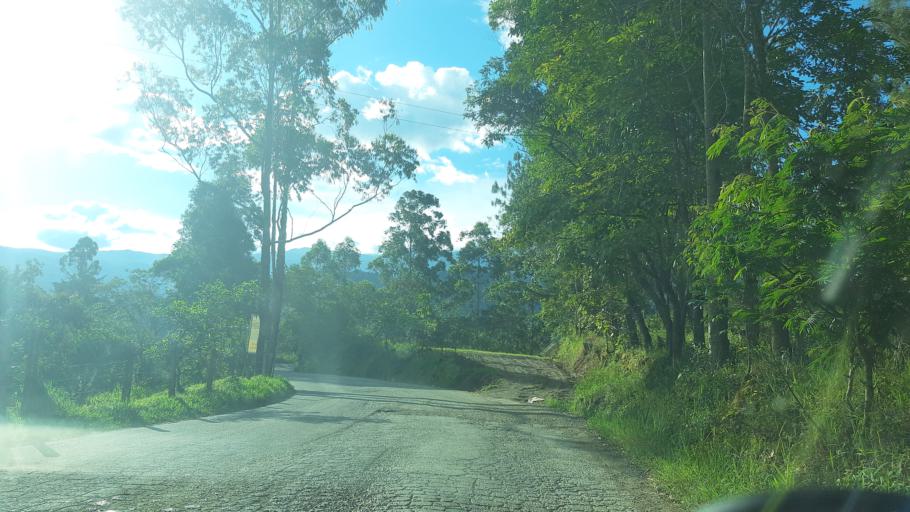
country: CO
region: Boyaca
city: Garagoa
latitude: 5.0744
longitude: -73.3774
